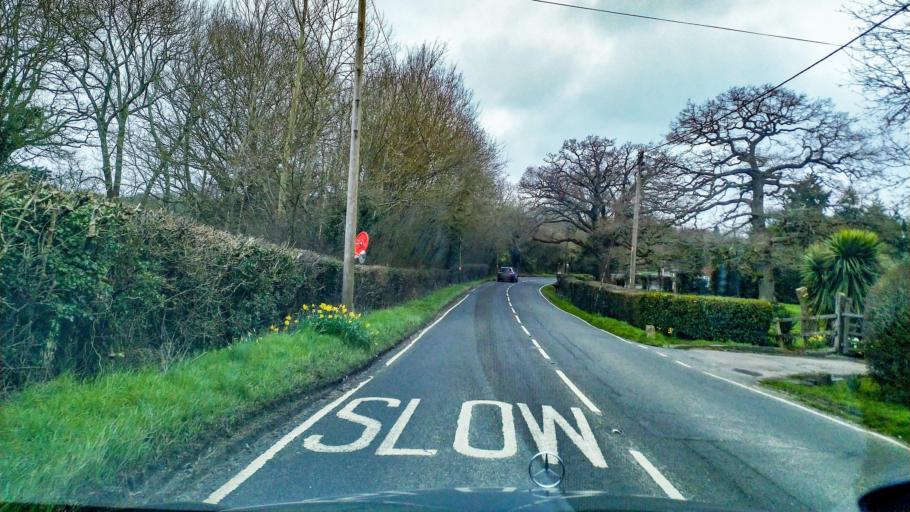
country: GB
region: England
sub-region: Surrey
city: Newdigate
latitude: 51.2079
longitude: -0.2774
